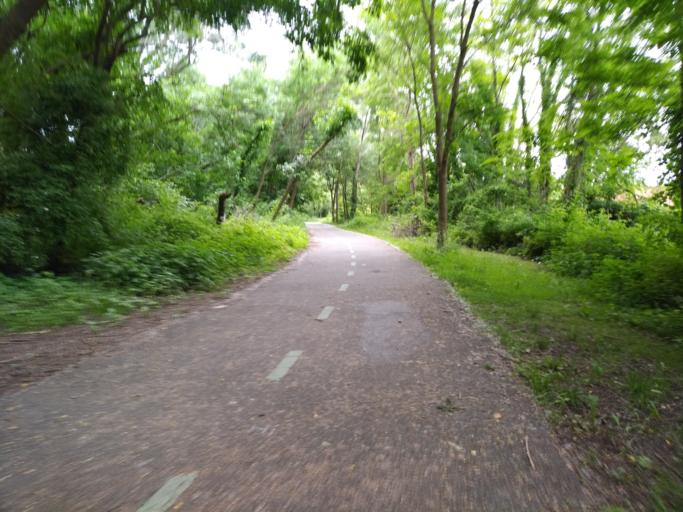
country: US
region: New York
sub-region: Queens County
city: Jamaica
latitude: 40.7466
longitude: -73.7958
